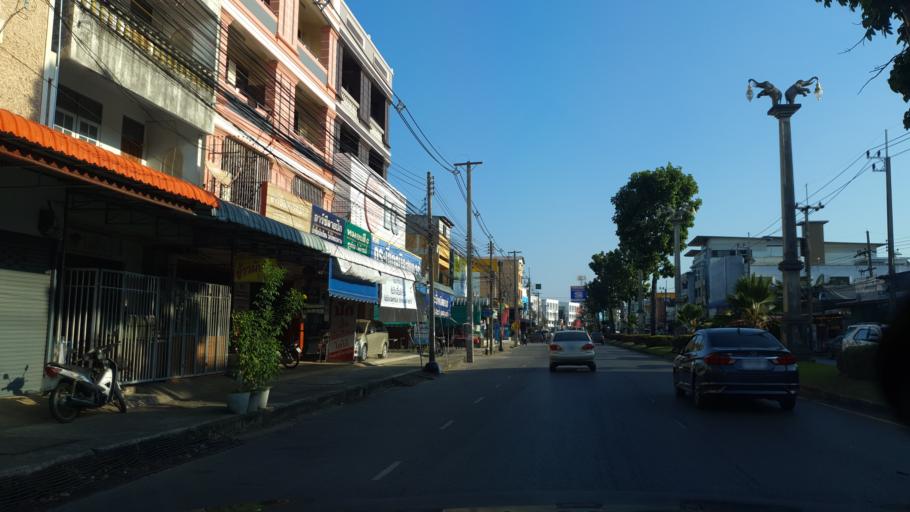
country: TH
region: Krabi
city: Krabi
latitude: 8.0691
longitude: 98.9136
